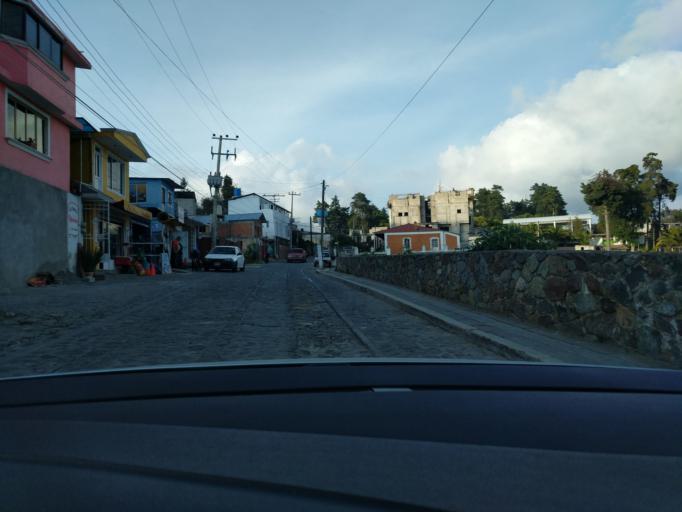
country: MX
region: Hidalgo
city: Mineral del Monte
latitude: 20.1431
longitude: -98.6733
